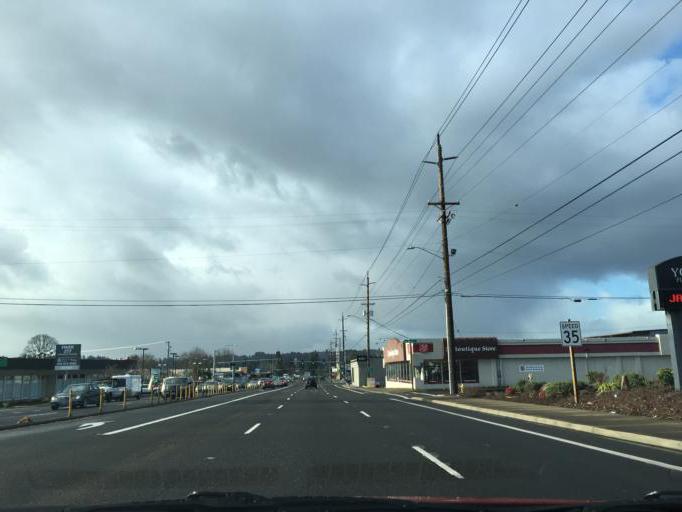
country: US
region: Oregon
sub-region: Washington County
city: Tigard
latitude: 45.4348
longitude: -122.7630
